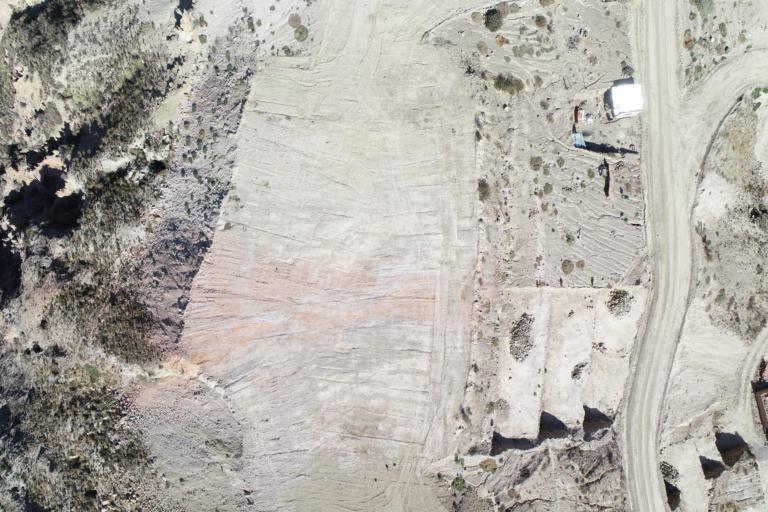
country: BO
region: La Paz
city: La Paz
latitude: -16.5491
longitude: -68.1068
